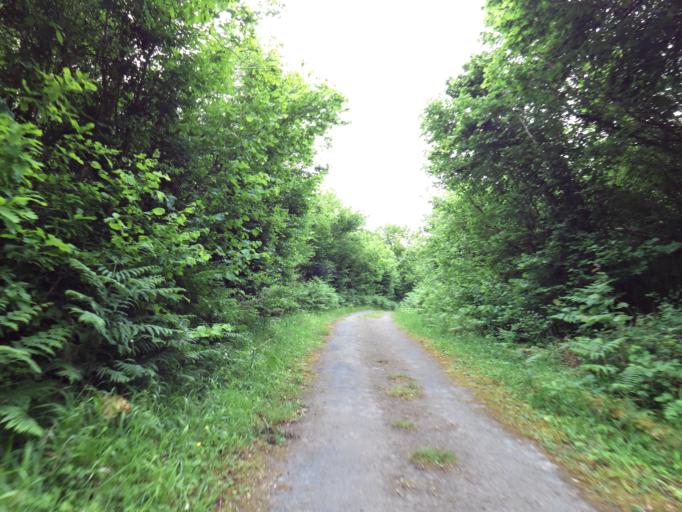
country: IE
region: Connaught
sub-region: County Galway
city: Gort
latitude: 53.0793
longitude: -8.8610
